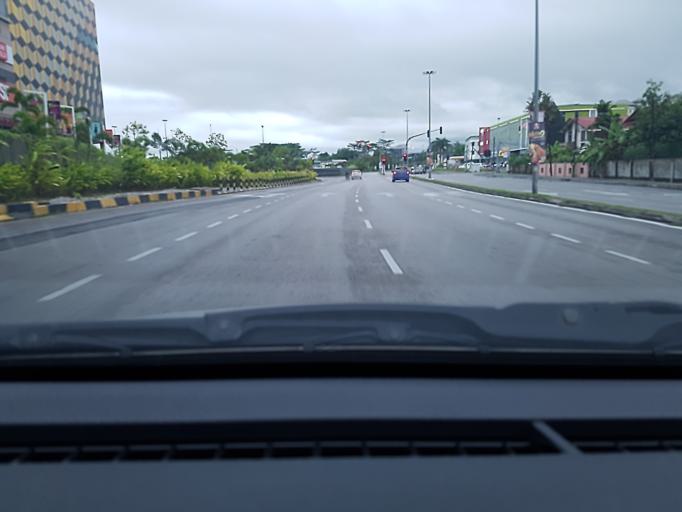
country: MY
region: Sarawak
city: Kuching
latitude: 1.5275
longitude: 110.3687
